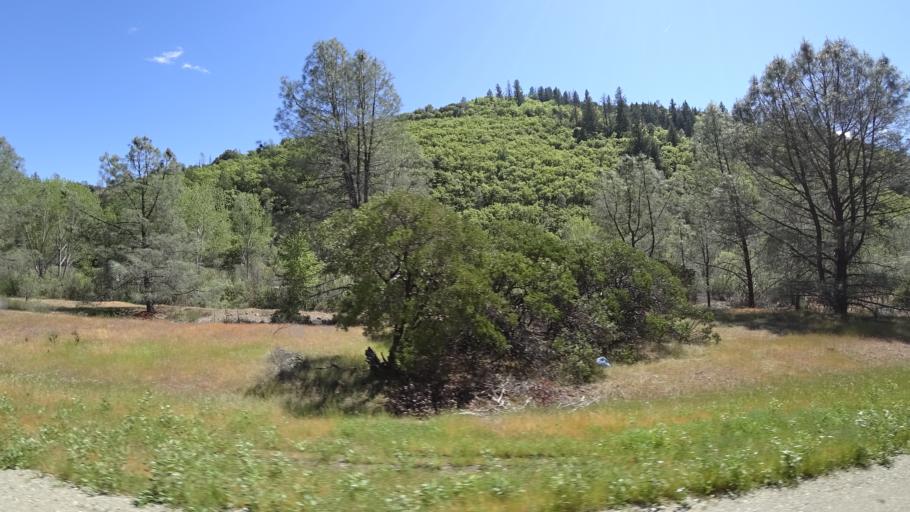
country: US
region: California
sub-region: Trinity County
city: Weaverville
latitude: 40.7318
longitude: -123.0254
